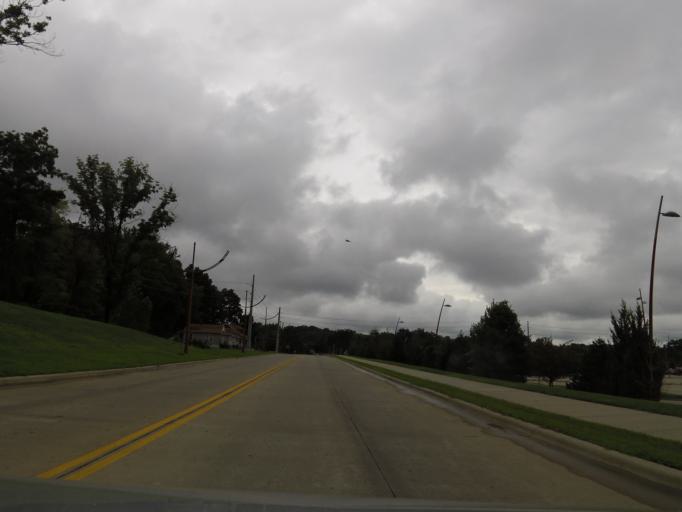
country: US
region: Missouri
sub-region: Cape Girardeau County
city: Cape Girardeau
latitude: 37.3132
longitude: -89.5190
